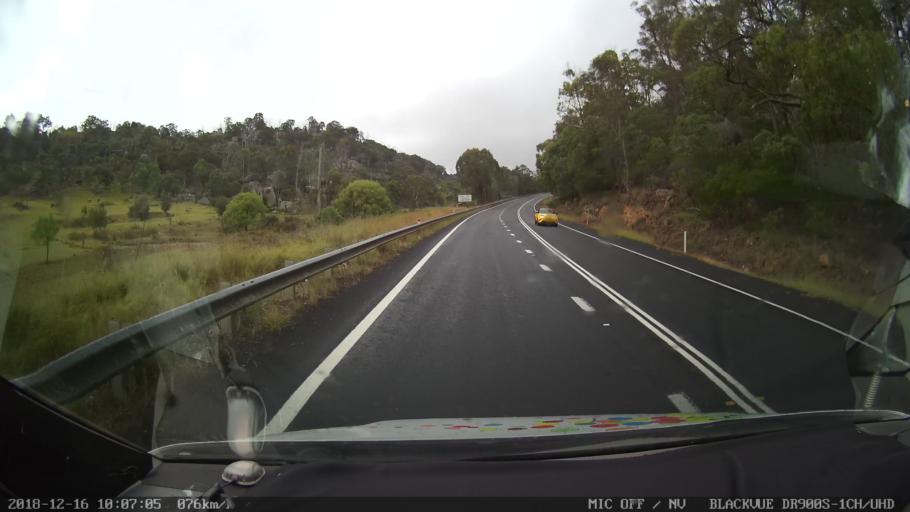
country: AU
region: New South Wales
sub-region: Glen Innes Severn
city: Glen Innes
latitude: -29.3382
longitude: 151.8936
